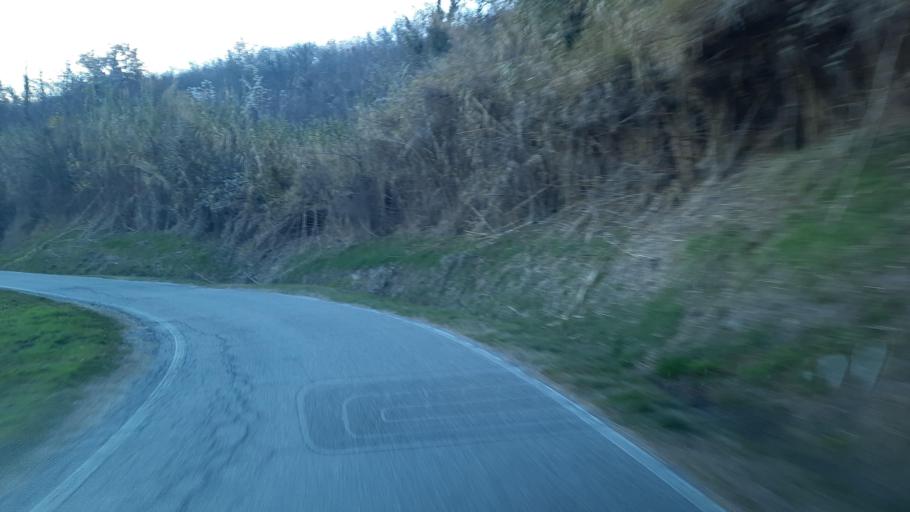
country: IT
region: Piedmont
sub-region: Provincia di Alessandria
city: Camino
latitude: 45.1625
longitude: 8.2752
